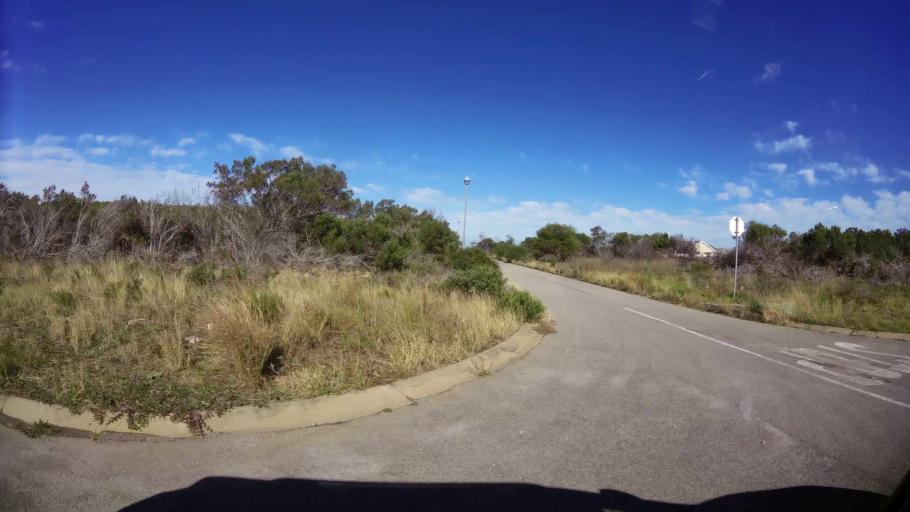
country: ZA
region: Eastern Cape
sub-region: Cacadu District Municipality
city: Jeffrey's Bay
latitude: -34.0321
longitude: 24.9075
